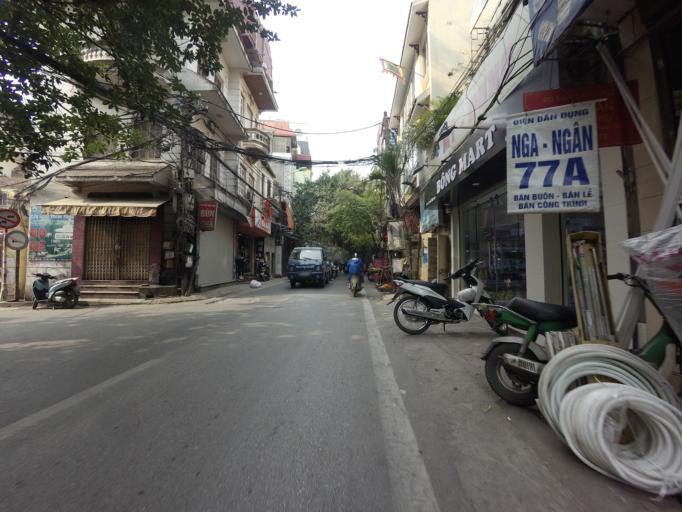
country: VN
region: Ha Noi
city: Hoan Kiem
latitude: 21.0522
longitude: 105.8372
